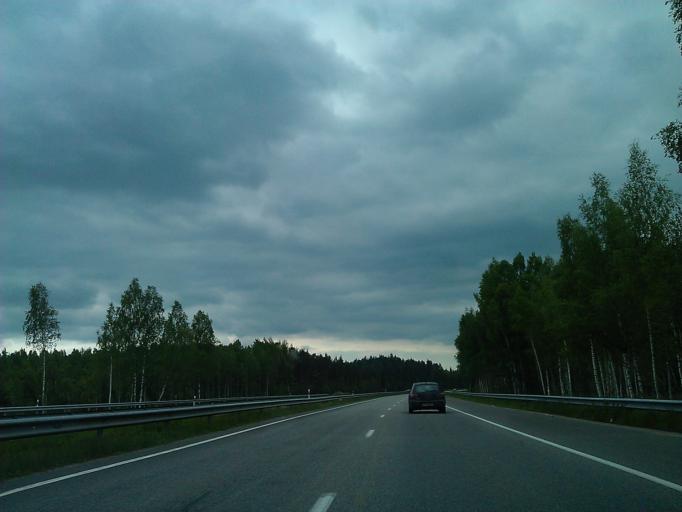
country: LV
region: Marupe
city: Marupe
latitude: 56.8525
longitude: 24.0626
